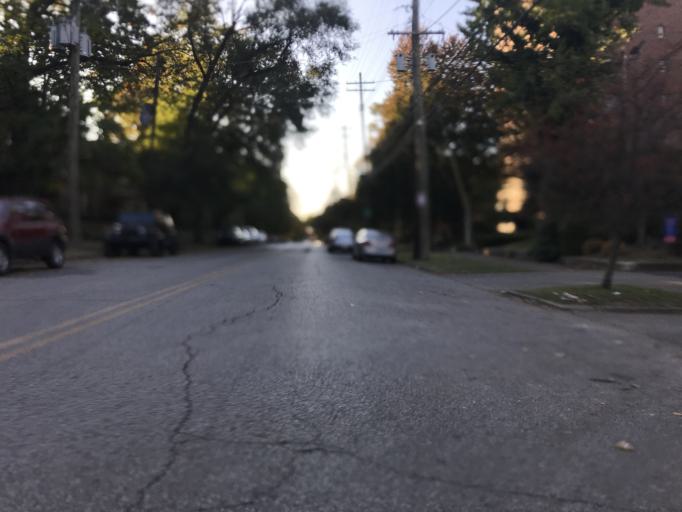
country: US
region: Kentucky
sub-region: Jefferson County
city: Louisville
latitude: 38.2329
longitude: -85.7615
